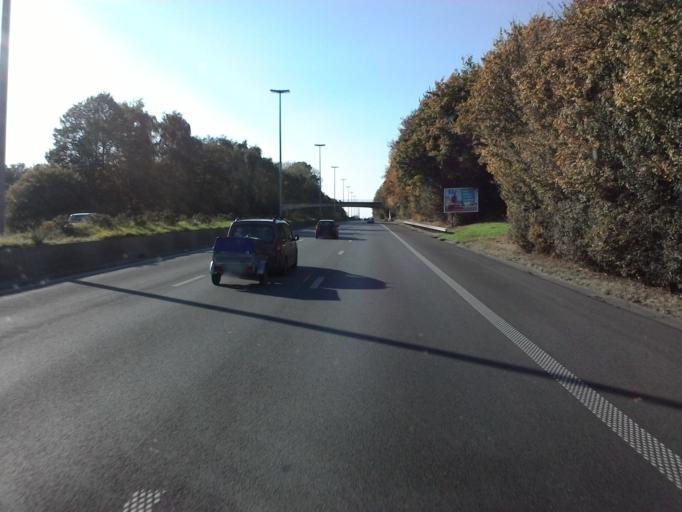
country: BE
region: Wallonia
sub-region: Province de Namur
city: Sombreffe
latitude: 50.4944
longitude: 4.6552
